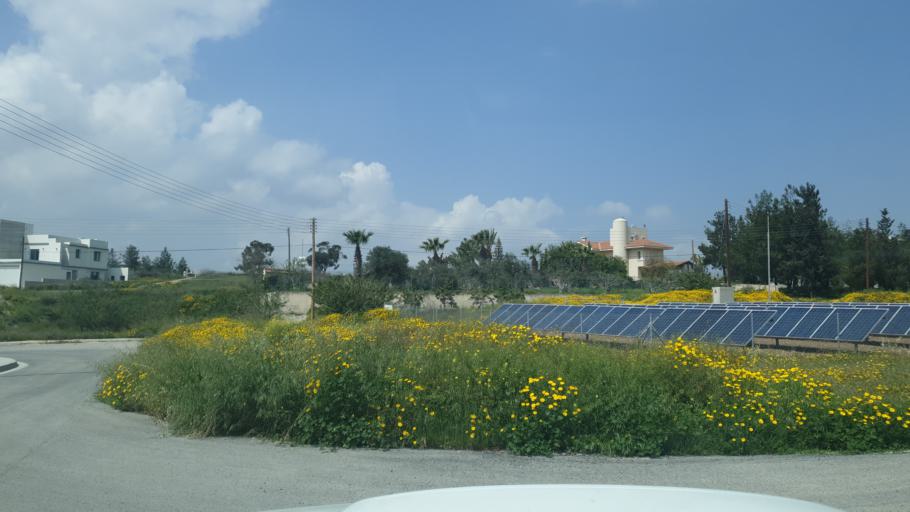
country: CY
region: Lefkosia
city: Geri
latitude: 35.1120
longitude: 33.4182
